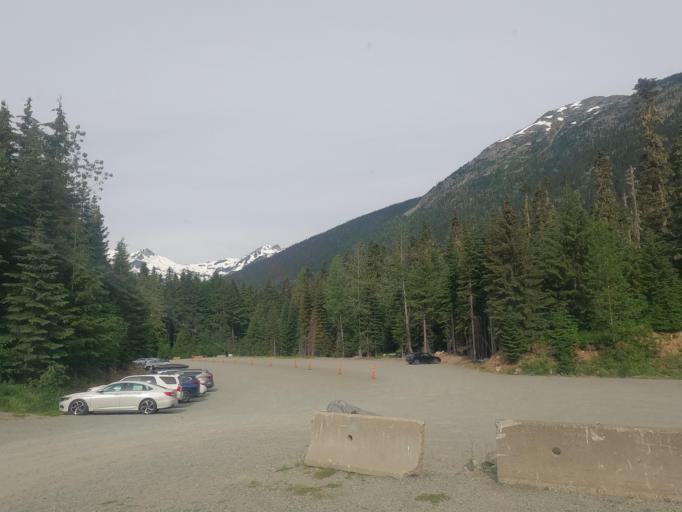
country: CA
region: British Columbia
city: Pemberton
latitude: 50.3697
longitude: -122.5034
